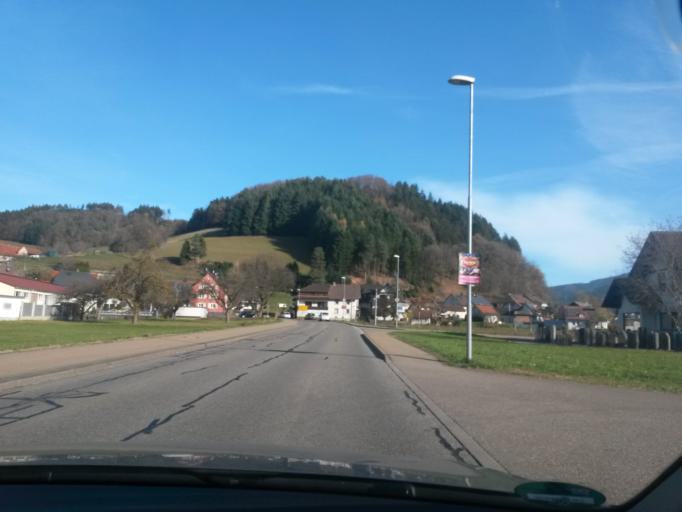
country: DE
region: Baden-Wuerttemberg
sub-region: Freiburg Region
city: Elzach
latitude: 48.1524
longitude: 8.0376
